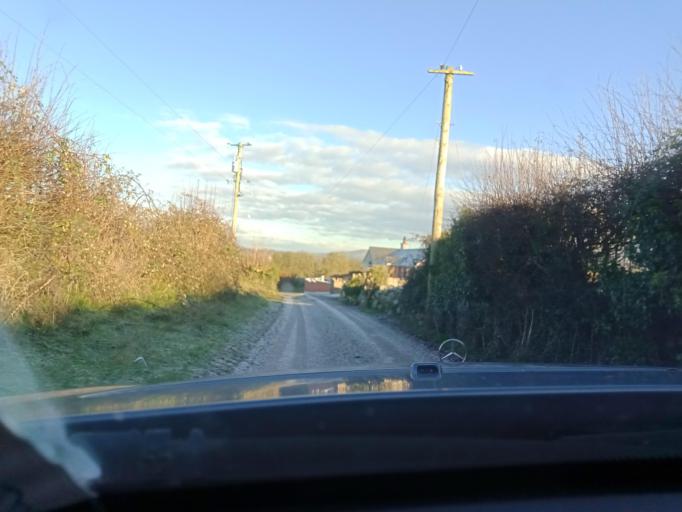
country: IE
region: Leinster
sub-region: Kilkenny
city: Graiguenamanagh
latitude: 52.5632
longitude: -6.9406
